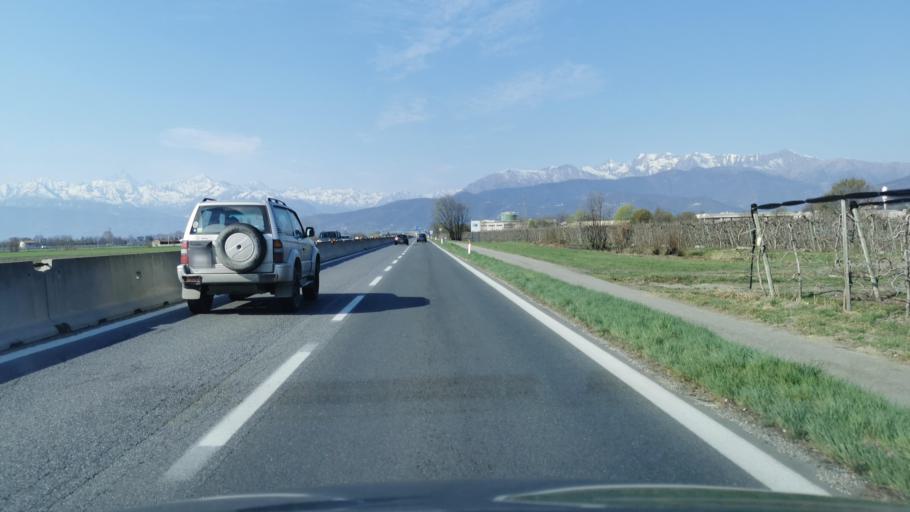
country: IT
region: Piedmont
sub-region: Provincia di Torino
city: Riva
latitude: 44.8855
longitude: 7.3711
